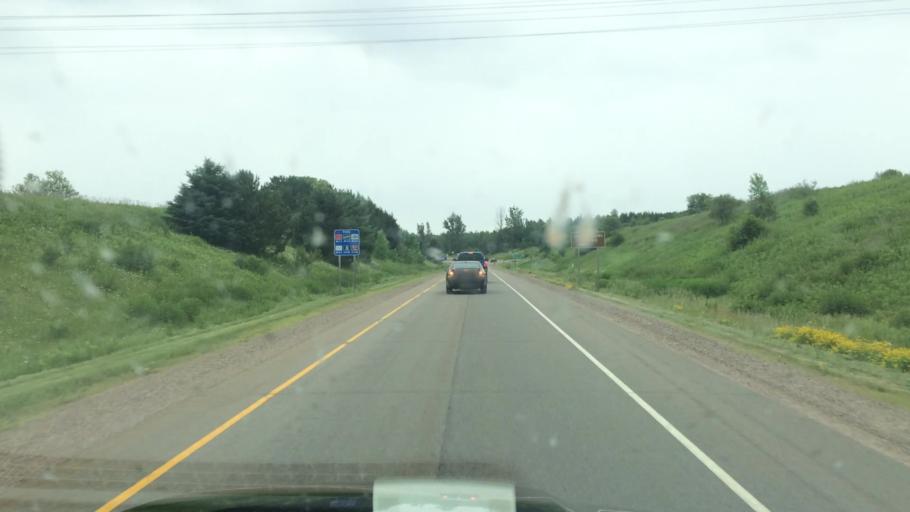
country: US
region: Wisconsin
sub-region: Lincoln County
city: Merrill
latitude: 45.1748
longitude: -89.6459
